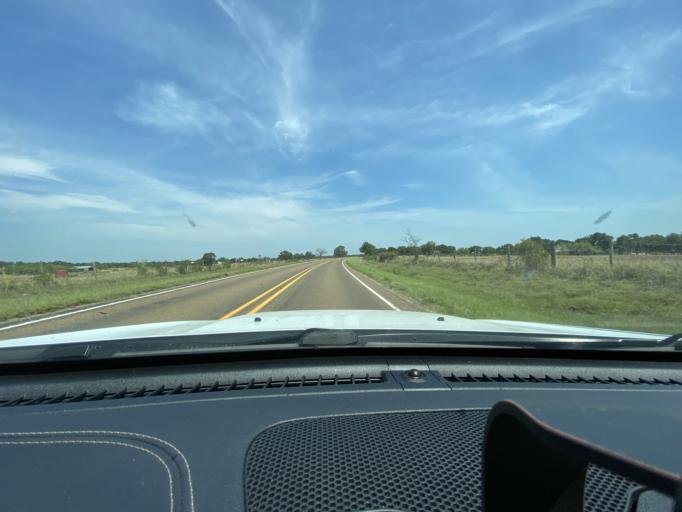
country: US
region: Texas
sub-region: Bastrop County
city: Smithville
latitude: 30.1137
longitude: -97.0810
